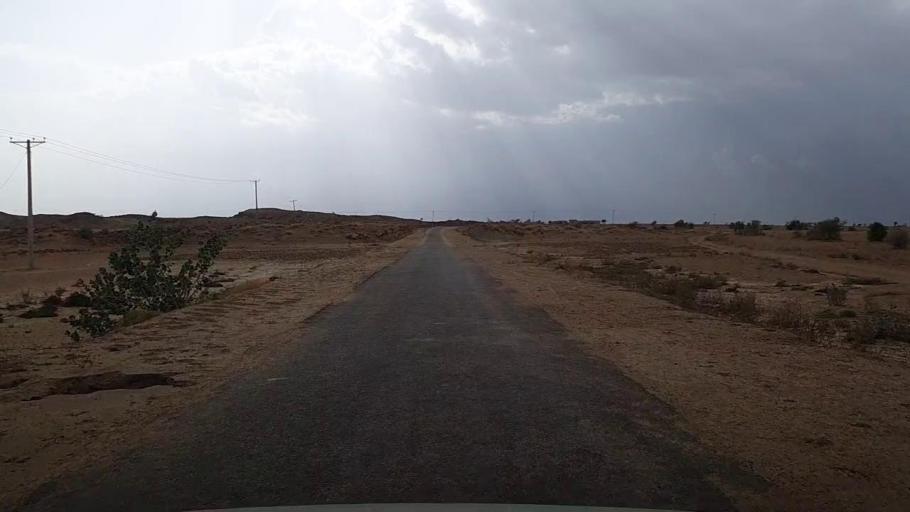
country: PK
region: Sindh
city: Jamshoro
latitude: 25.4996
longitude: 67.6380
